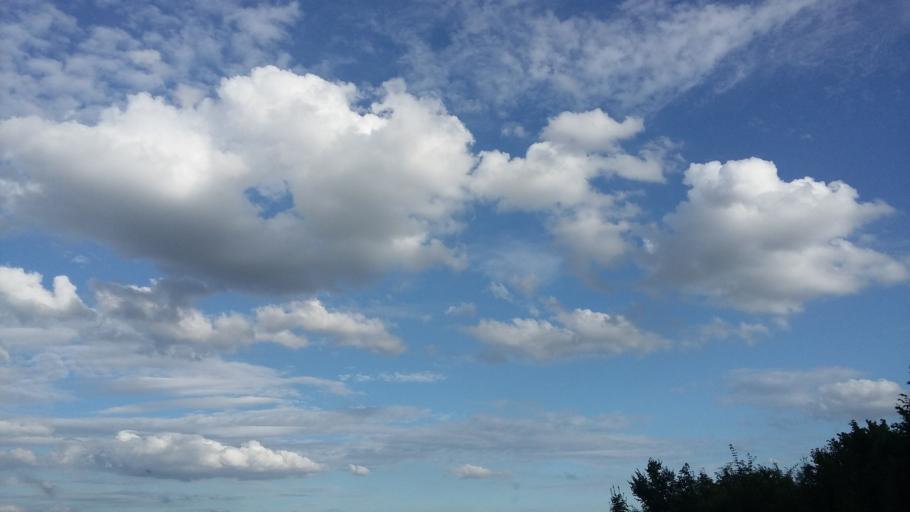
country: DE
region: Bavaria
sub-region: Swabia
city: Merching
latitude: 48.2427
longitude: 10.9964
